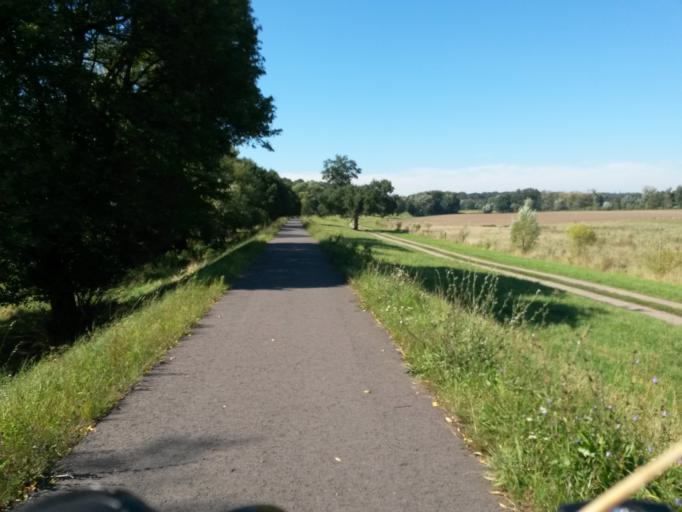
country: DE
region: Brandenburg
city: Schoneberg
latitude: 52.9421
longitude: 14.1167
